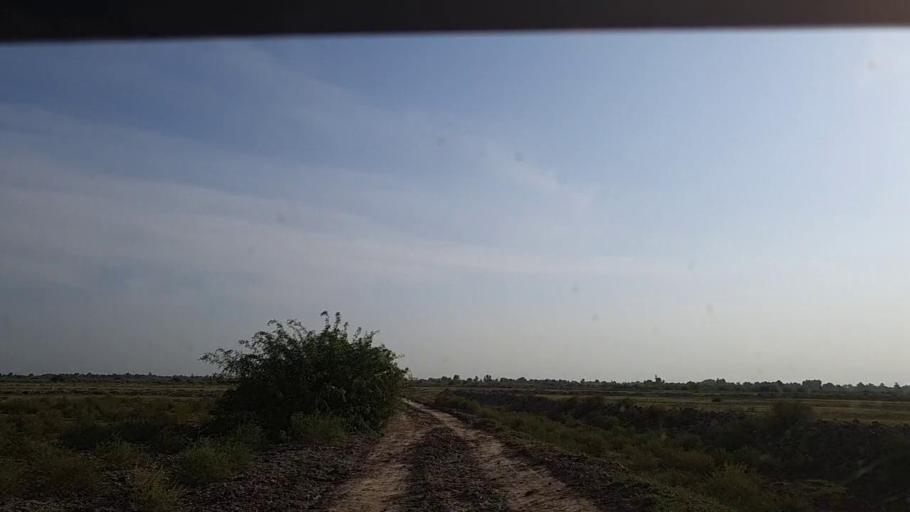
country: PK
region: Sindh
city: Adilpur
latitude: 27.9095
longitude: 69.2132
